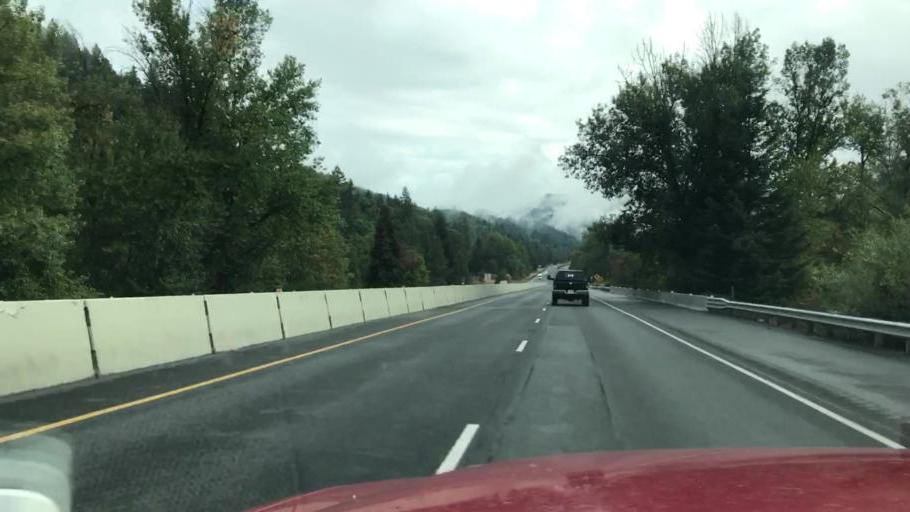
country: US
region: Oregon
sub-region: Josephine County
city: Merlin
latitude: 42.6959
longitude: -123.3876
